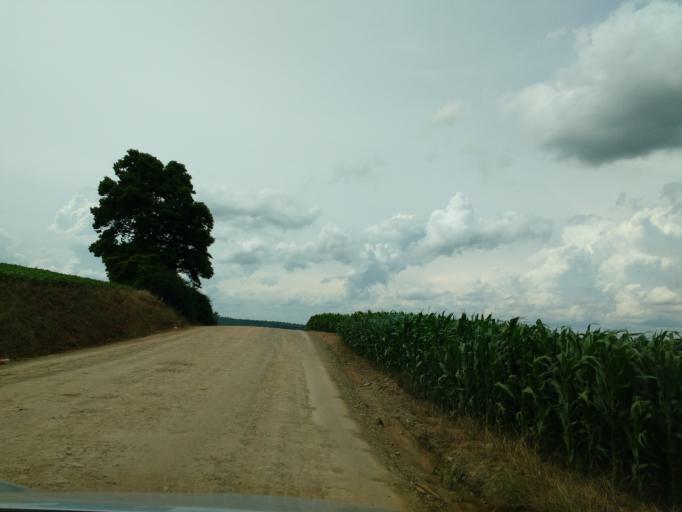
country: BR
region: Parana
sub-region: Prudentopolis
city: Prudentopolis
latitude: -25.0961
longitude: -51.0150
